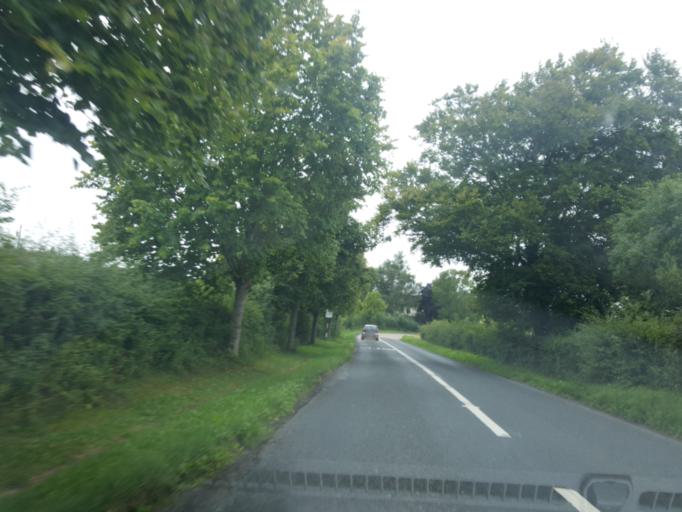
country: IE
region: Leinster
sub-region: Kildare
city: Kilcullen
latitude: 53.1263
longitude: -6.7385
